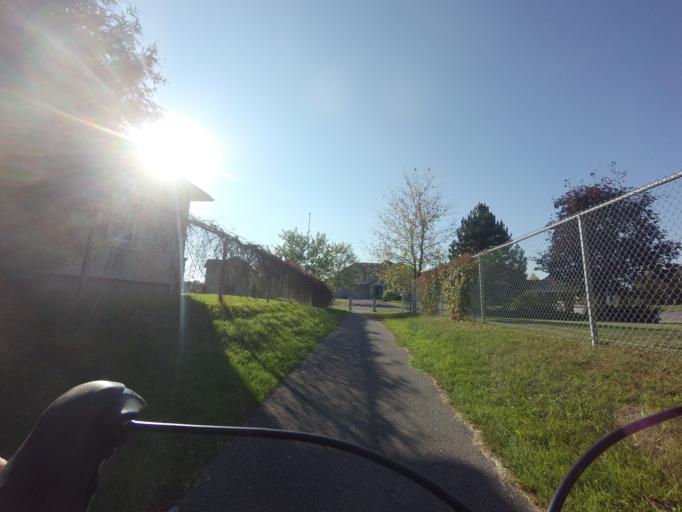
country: CA
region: Ontario
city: Bells Corners
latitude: 45.2250
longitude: -75.6952
